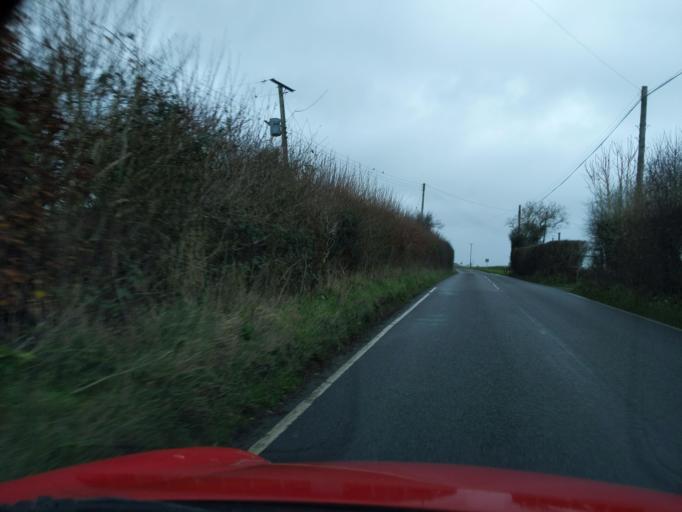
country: GB
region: England
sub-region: Cornwall
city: Boyton
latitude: 50.7320
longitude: -4.3254
